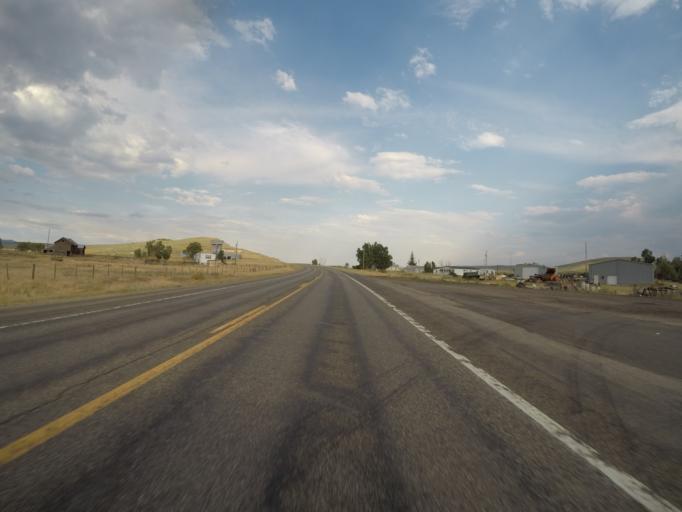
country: US
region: Colorado
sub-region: Moffat County
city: Craig
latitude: 40.5269
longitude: -107.4290
